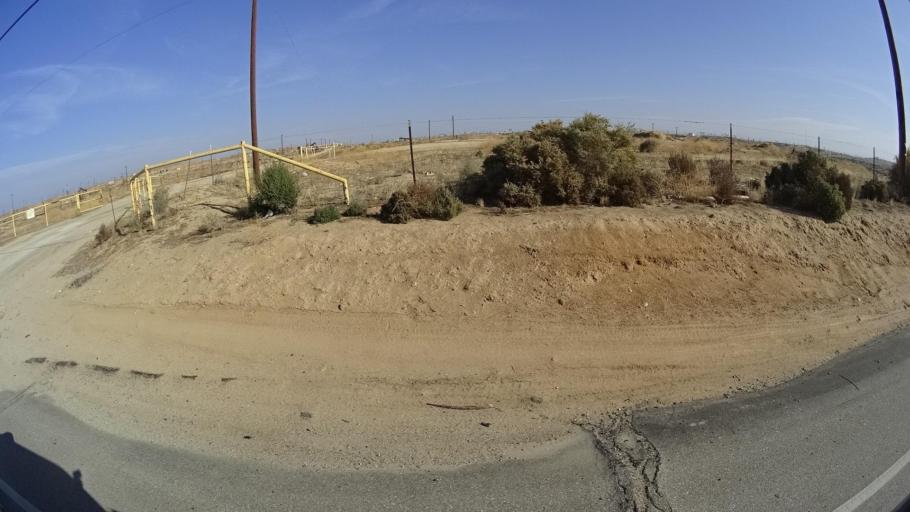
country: US
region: California
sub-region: Kern County
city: Oildale
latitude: 35.4626
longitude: -119.0536
